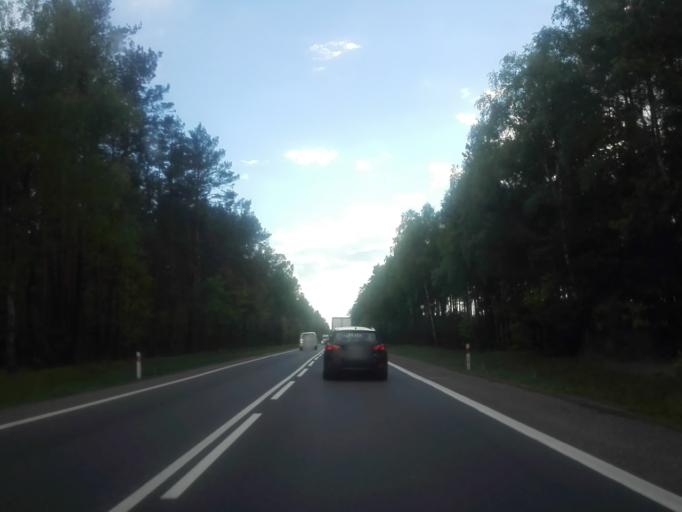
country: PL
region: Masovian Voivodeship
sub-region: Powiat wyszkowski
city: Dlugosiodlo
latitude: 52.6948
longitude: 21.6546
